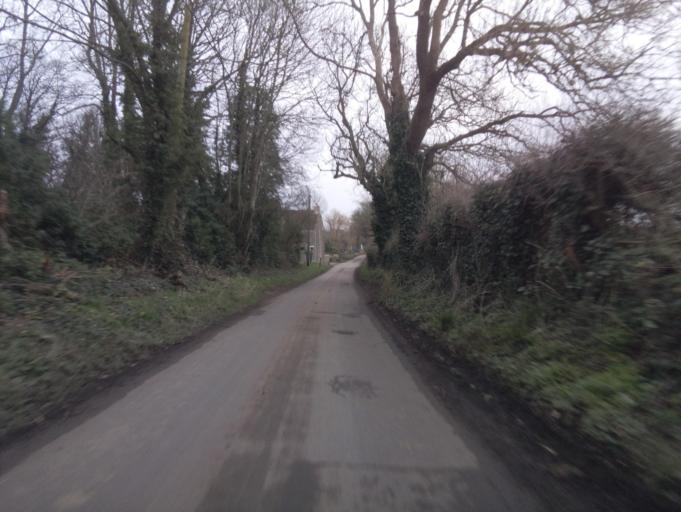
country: GB
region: England
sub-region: Wiltshire
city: Nettleton
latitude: 51.5003
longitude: -2.2591
